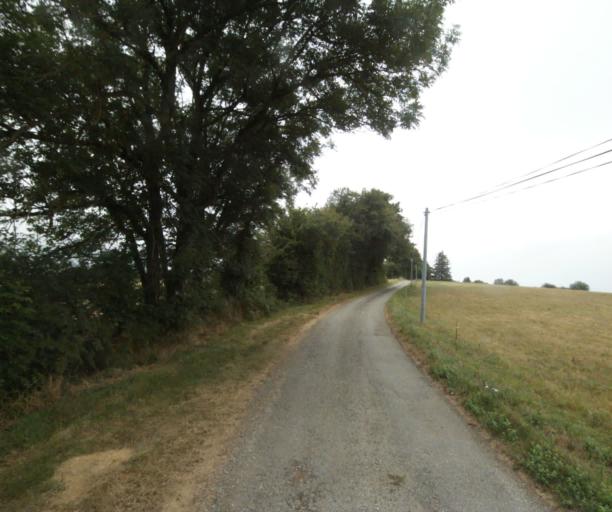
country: FR
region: Midi-Pyrenees
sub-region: Departement du Tarn
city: Soreze
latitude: 43.4144
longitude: 2.0438
